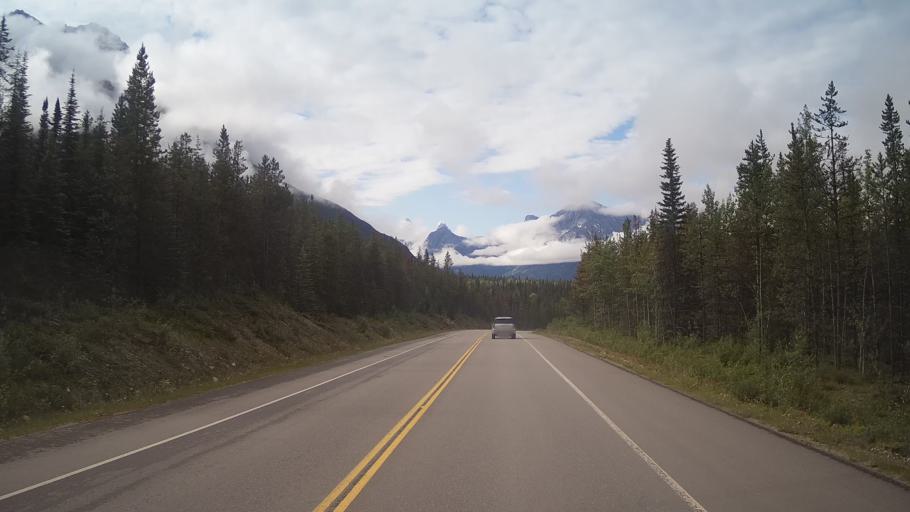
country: CA
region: Alberta
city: Jasper Park Lodge
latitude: 52.6875
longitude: -117.8657
